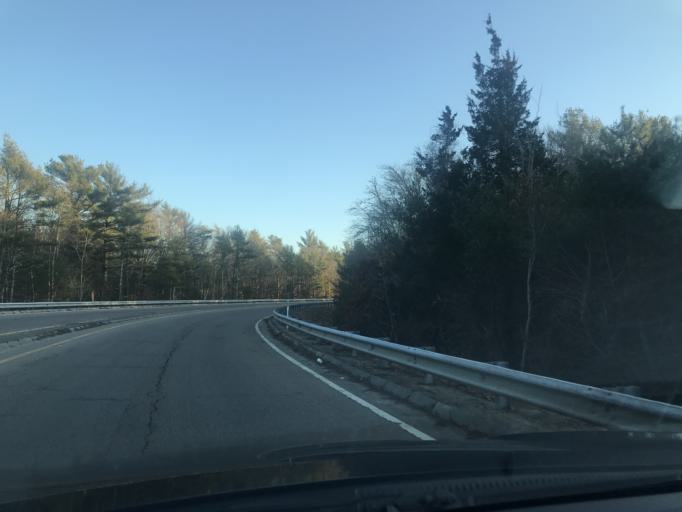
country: US
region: Massachusetts
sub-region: Plymouth County
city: Middleborough Center
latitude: 41.8478
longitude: -70.8481
